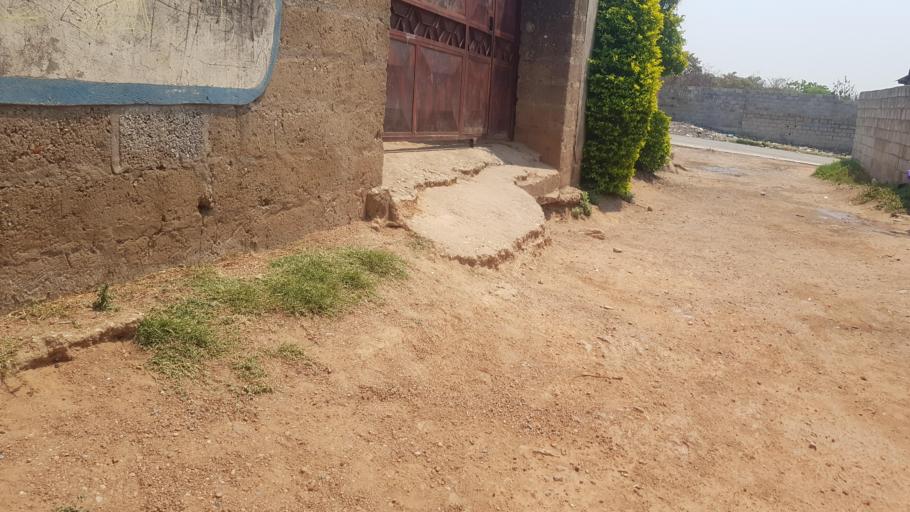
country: ZM
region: Lusaka
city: Lusaka
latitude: -15.4386
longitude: 28.3833
